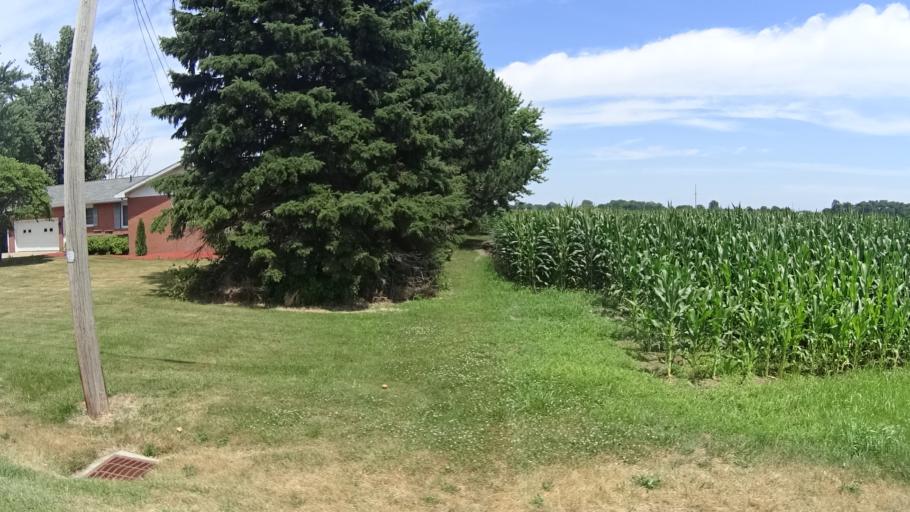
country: US
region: Ohio
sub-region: Erie County
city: Sandusky
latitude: 41.3831
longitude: -82.7705
